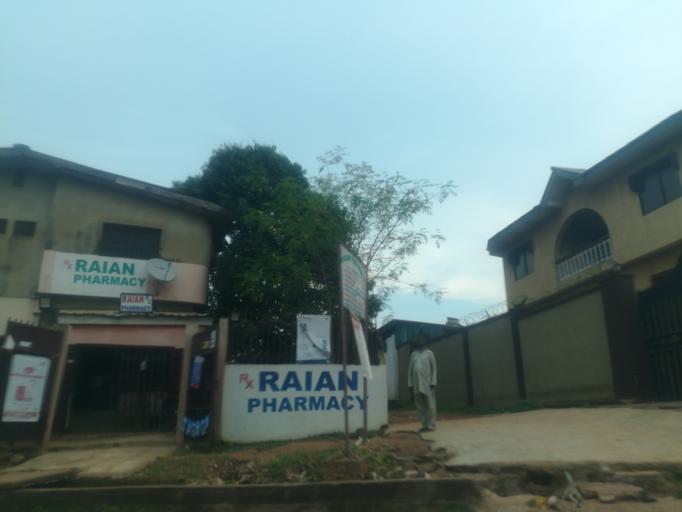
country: NG
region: Oyo
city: Ibadan
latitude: 7.4374
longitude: 3.9234
